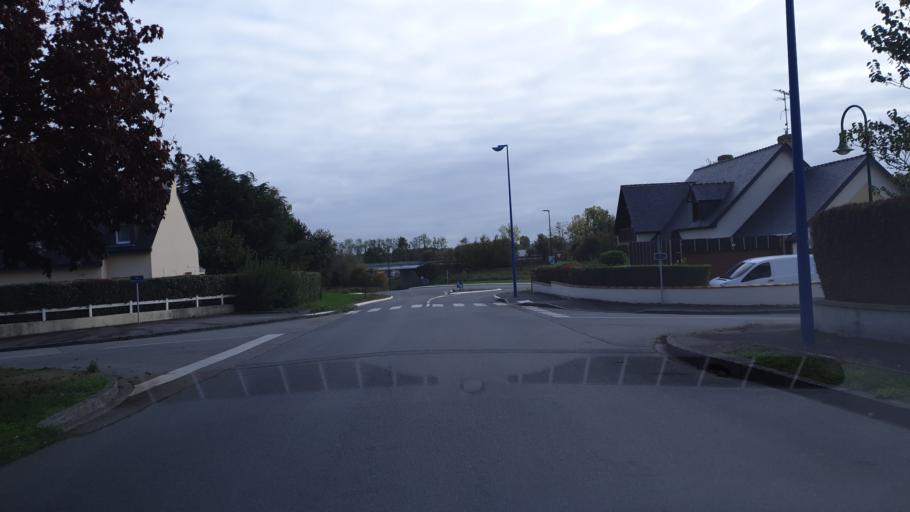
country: FR
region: Brittany
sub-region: Departement d'Ille-et-Vilaine
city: Janze
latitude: 47.9606
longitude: -1.4884
